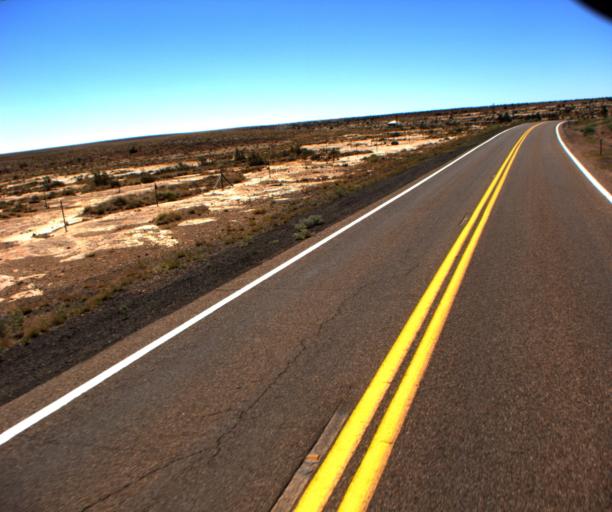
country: US
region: Arizona
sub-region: Navajo County
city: Winslow
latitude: 34.9715
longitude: -110.6484
